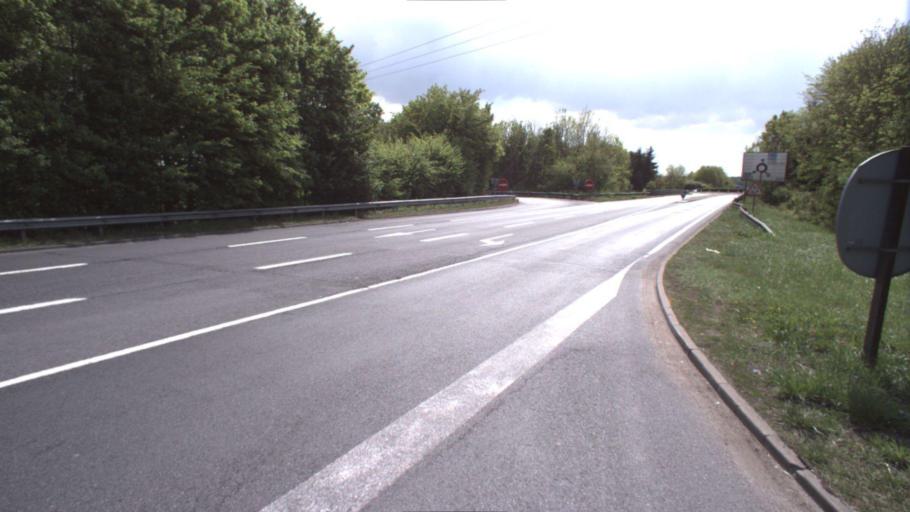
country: FR
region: Ile-de-France
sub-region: Departement de Seine-et-Marne
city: Fontenay-Tresigny
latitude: 48.7190
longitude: 2.8477
